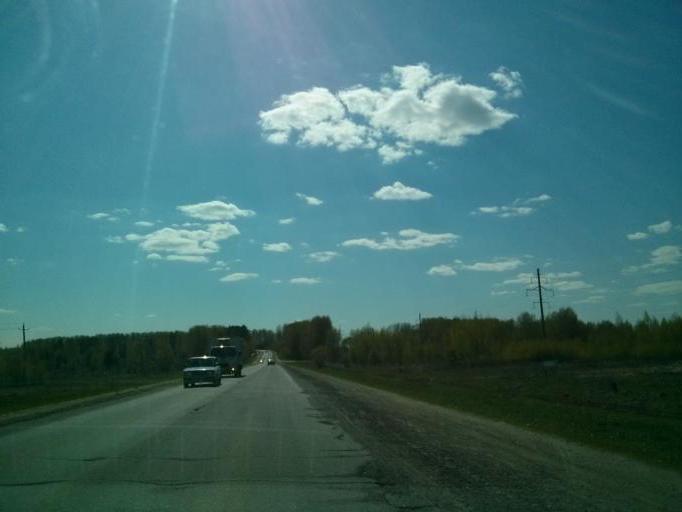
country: RU
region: Nizjnij Novgorod
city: Taremskoye
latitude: 55.9184
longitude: 43.0296
